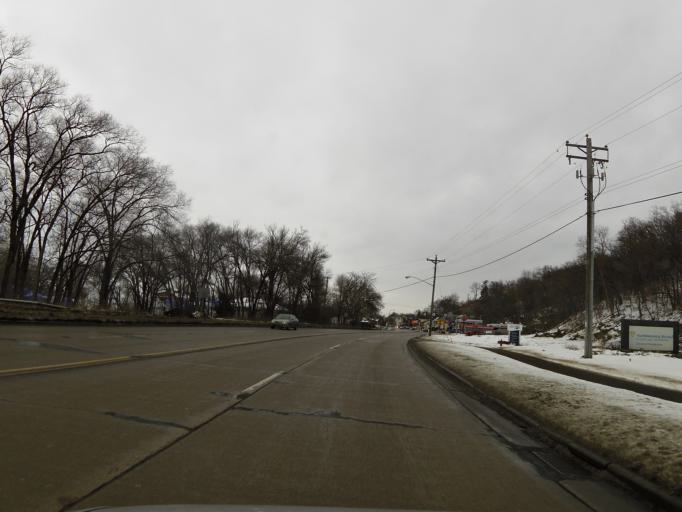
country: US
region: Wisconsin
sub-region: Saint Croix County
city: Hudson
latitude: 44.9691
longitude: -92.7567
